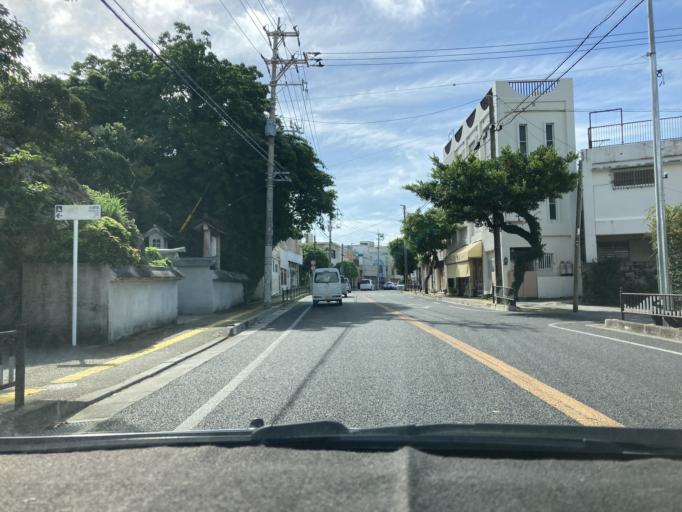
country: JP
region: Okinawa
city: Itoman
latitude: 26.1338
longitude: 127.6698
